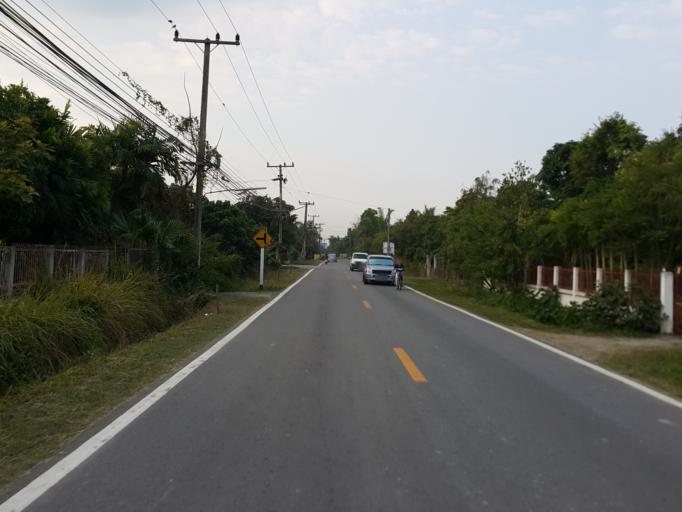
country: TH
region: Chiang Mai
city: San Sai
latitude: 18.8182
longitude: 99.0740
